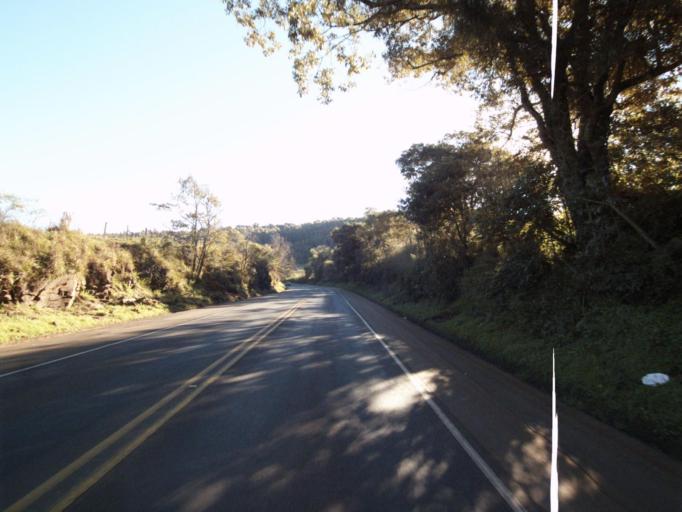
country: BR
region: Santa Catarina
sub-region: Chapeco
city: Chapeco
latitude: -26.9974
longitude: -52.7016
